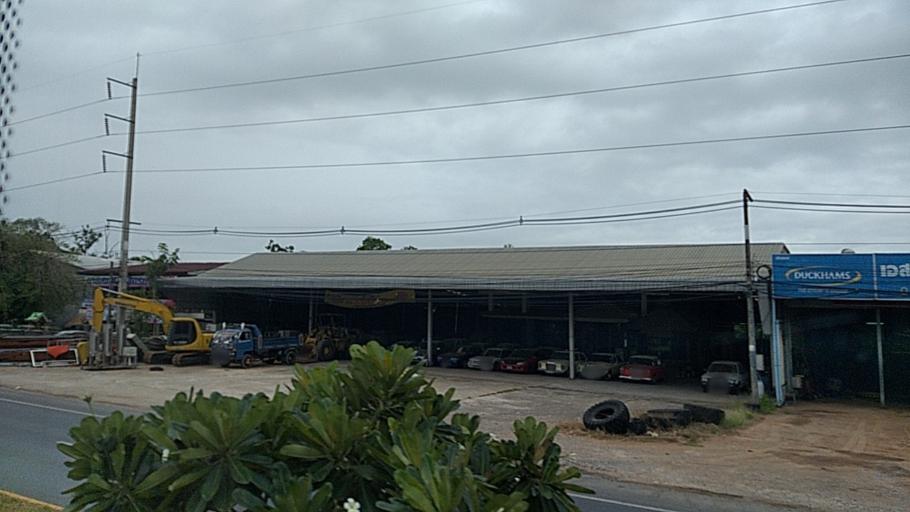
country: TH
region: Maha Sarakham
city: Maha Sarakham
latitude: 16.1628
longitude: 103.2824
